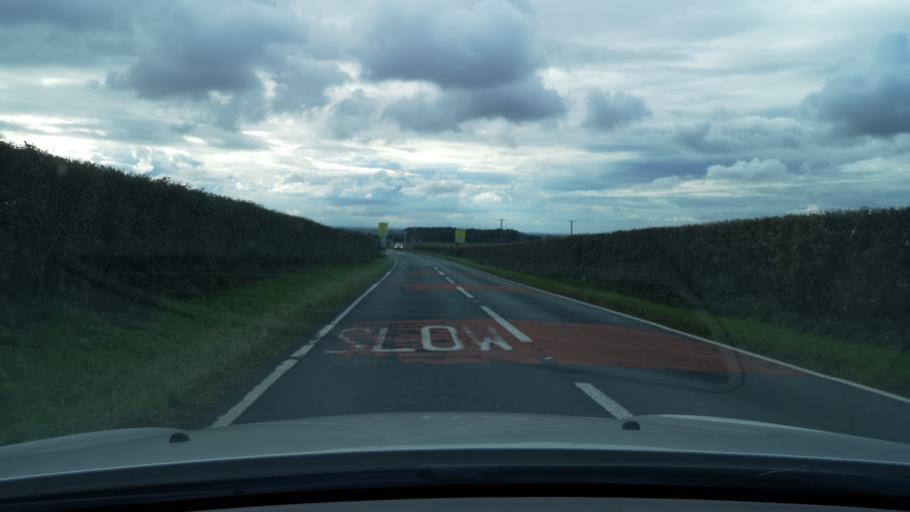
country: GB
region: England
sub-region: East Riding of Yorkshire
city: South Cave
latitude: 53.7943
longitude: -0.6104
